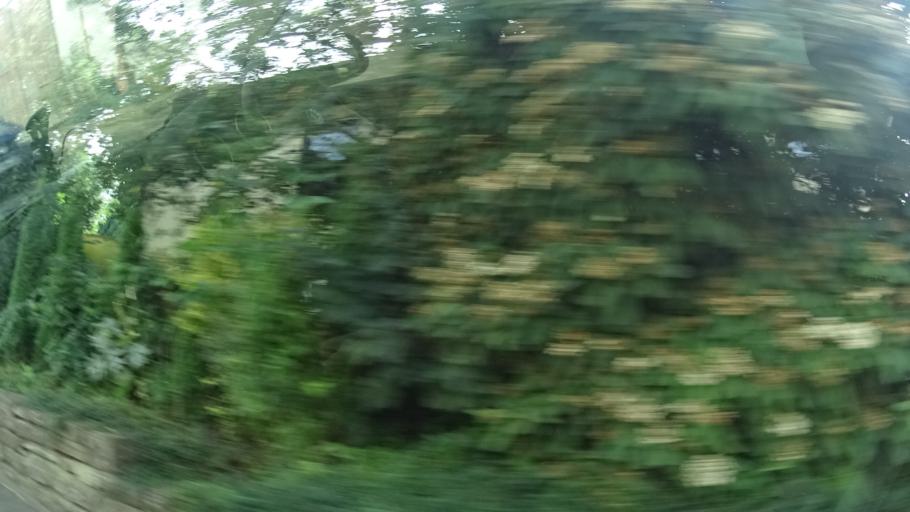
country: DE
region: Baden-Wuerttemberg
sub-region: Karlsruhe Region
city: Hardheim
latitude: 49.6479
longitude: 9.4849
